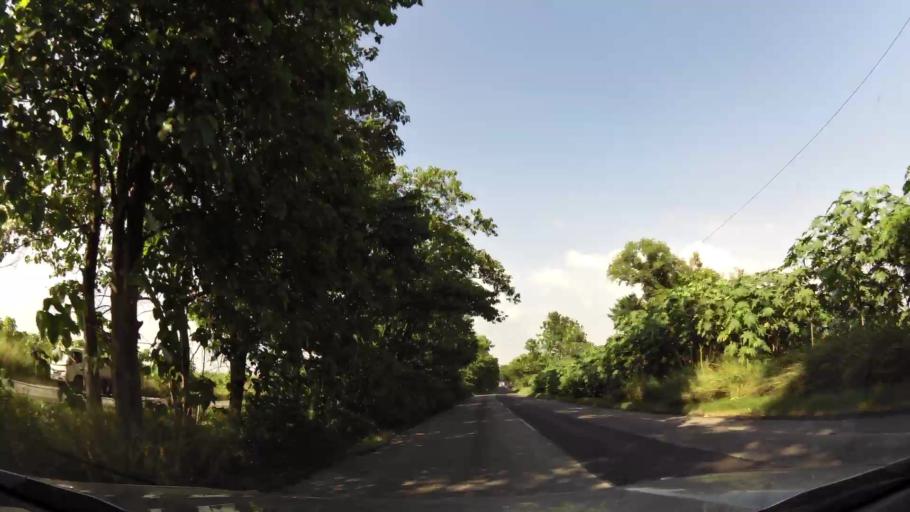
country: GT
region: Escuintla
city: Puerto San Jose
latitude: 13.9888
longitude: -90.7884
